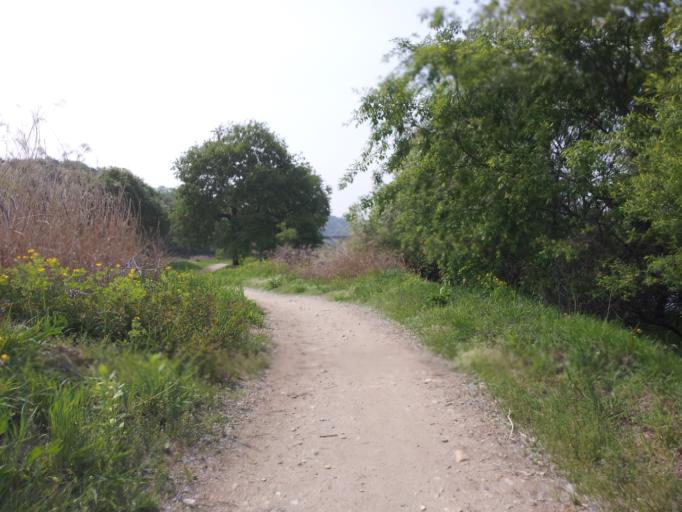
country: KR
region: Daejeon
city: Daejeon
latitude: 36.3374
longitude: 127.3540
